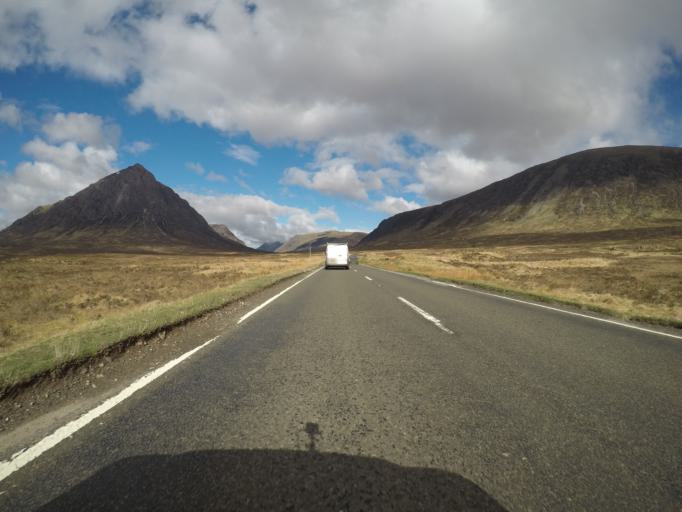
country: GB
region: Scotland
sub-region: Highland
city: Spean Bridge
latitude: 56.6523
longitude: -4.8549
